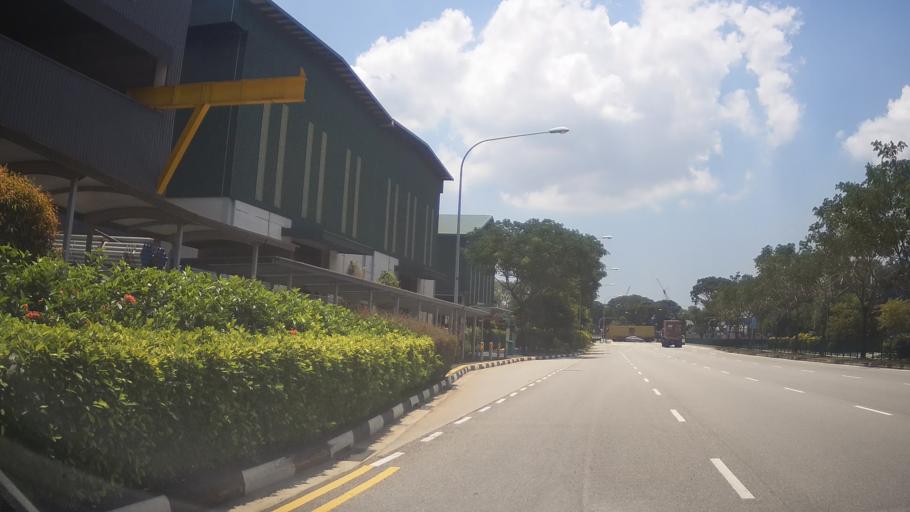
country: SG
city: Singapore
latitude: 1.3116
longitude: 103.6788
